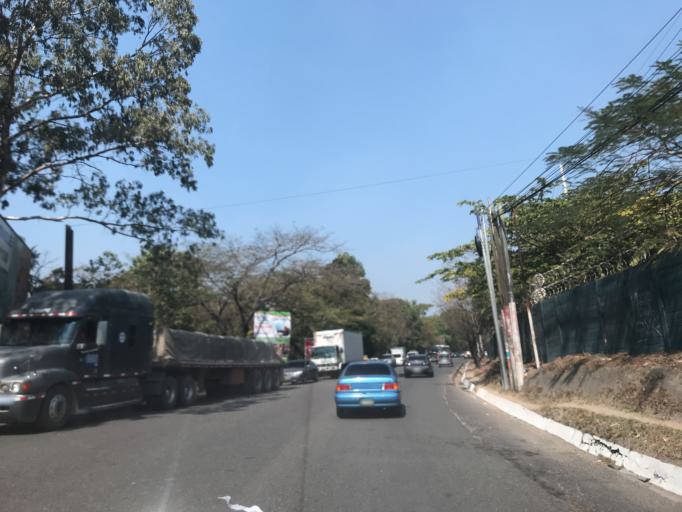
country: GT
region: Guatemala
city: Petapa
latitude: 14.5340
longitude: -90.5565
